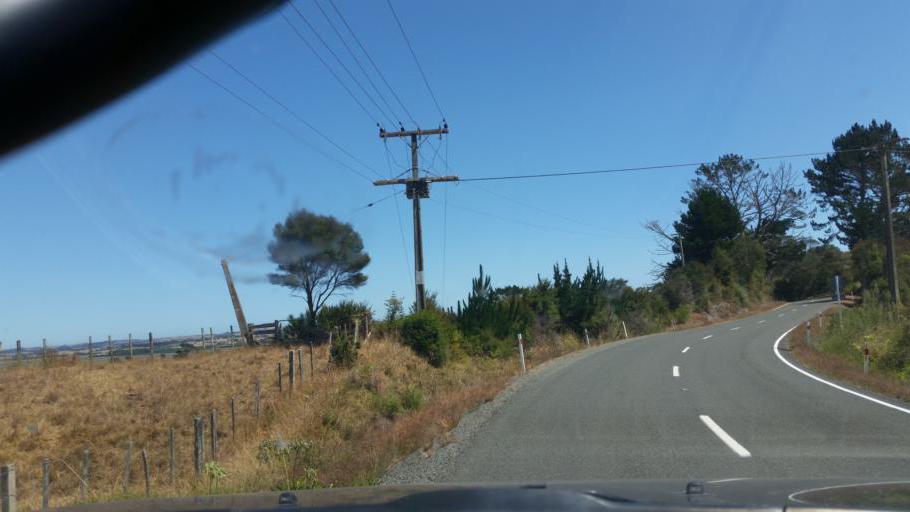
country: NZ
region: Northland
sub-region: Kaipara District
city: Dargaville
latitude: -36.0091
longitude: 173.9442
